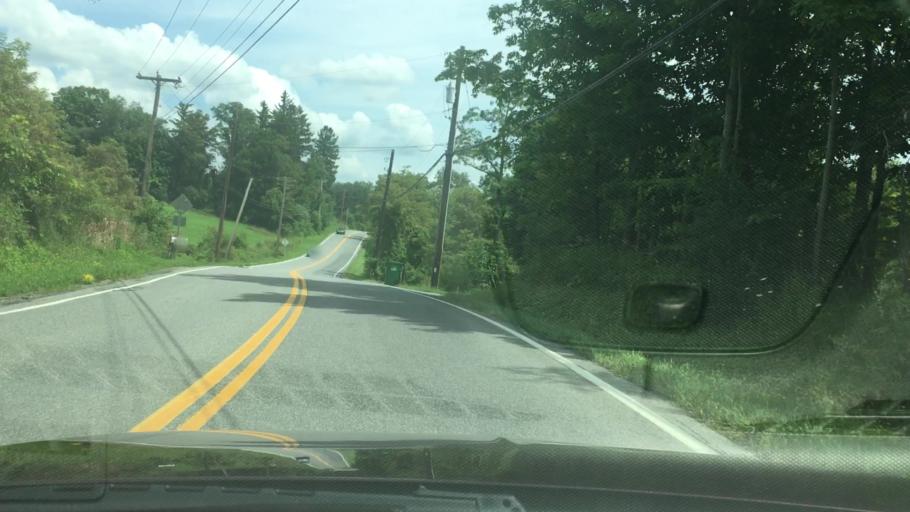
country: US
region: New York
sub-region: Dutchess County
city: Red Oaks Mill
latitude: 41.6506
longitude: -73.8305
